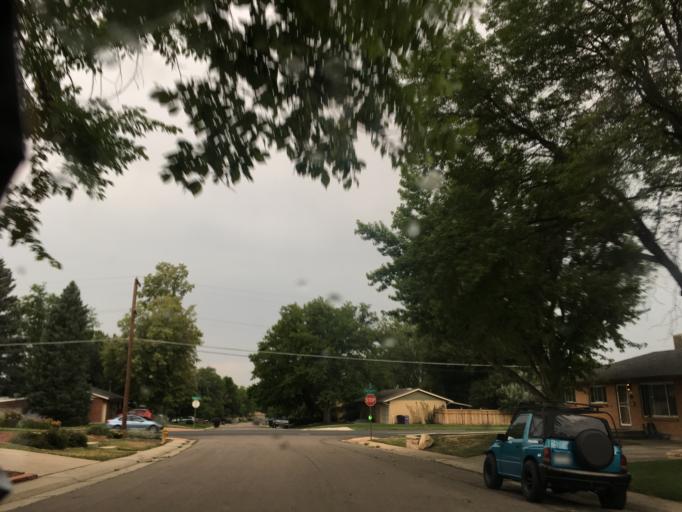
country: US
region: Colorado
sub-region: Arapahoe County
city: Sheridan
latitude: 39.6616
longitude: -105.0393
